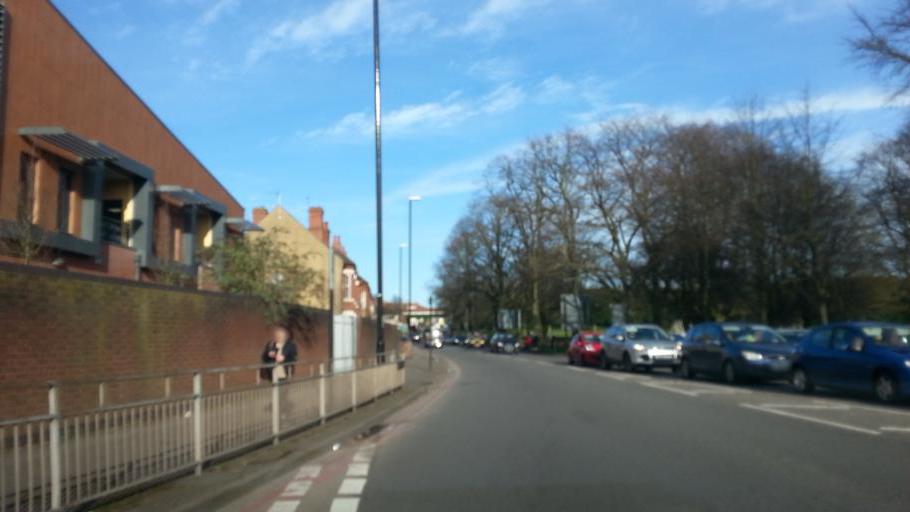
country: GB
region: England
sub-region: Coventry
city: Coventry
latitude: 52.4087
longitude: -1.4916
